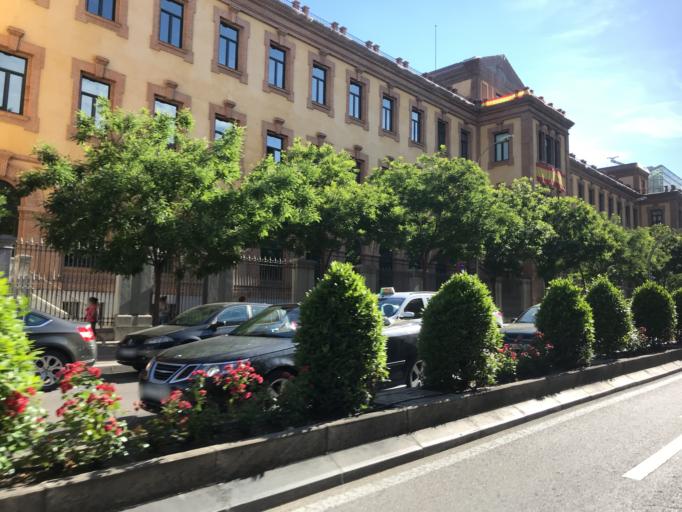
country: ES
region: Madrid
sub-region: Provincia de Madrid
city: Salamanca
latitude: 40.4212
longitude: -3.6704
